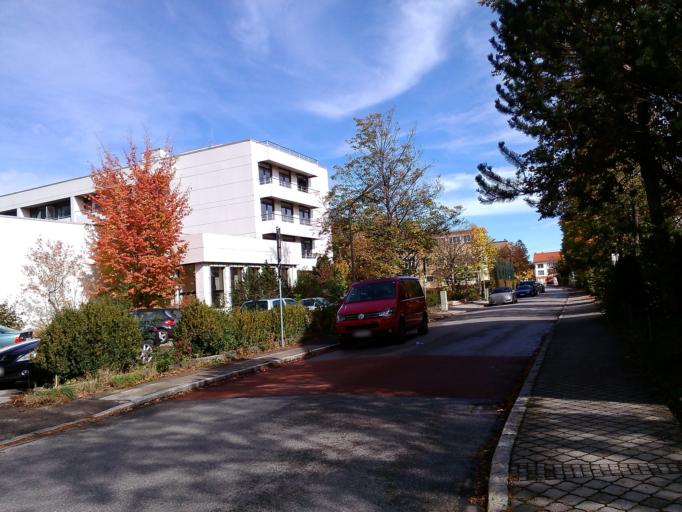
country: DE
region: Bavaria
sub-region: Upper Bavaria
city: Gauting
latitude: 48.0653
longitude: 11.3775
